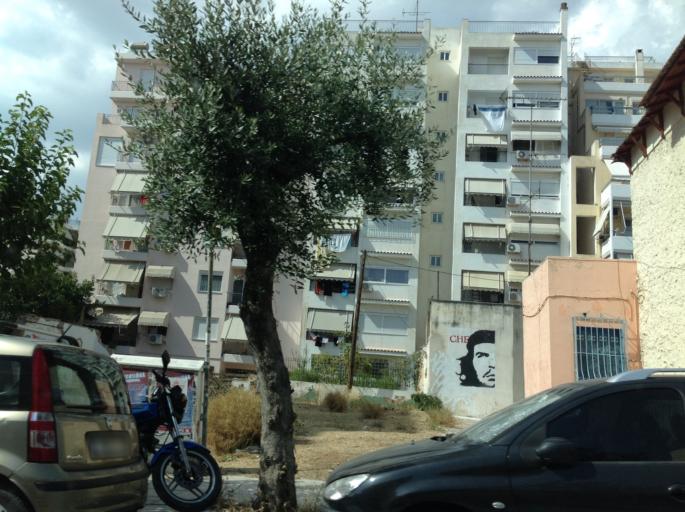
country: GR
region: Attica
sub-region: Nomarchia Athinas
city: Kaisariani
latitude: 37.9678
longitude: 23.7617
